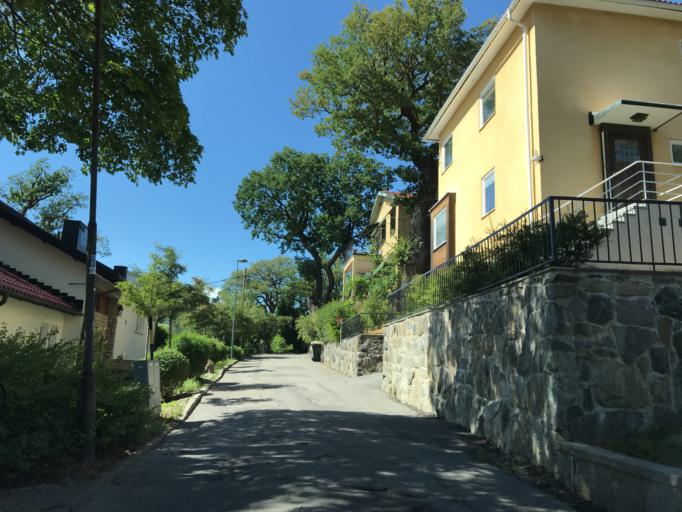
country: SE
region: Stockholm
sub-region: Solna Kommun
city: Solna
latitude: 59.3173
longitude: 17.9848
